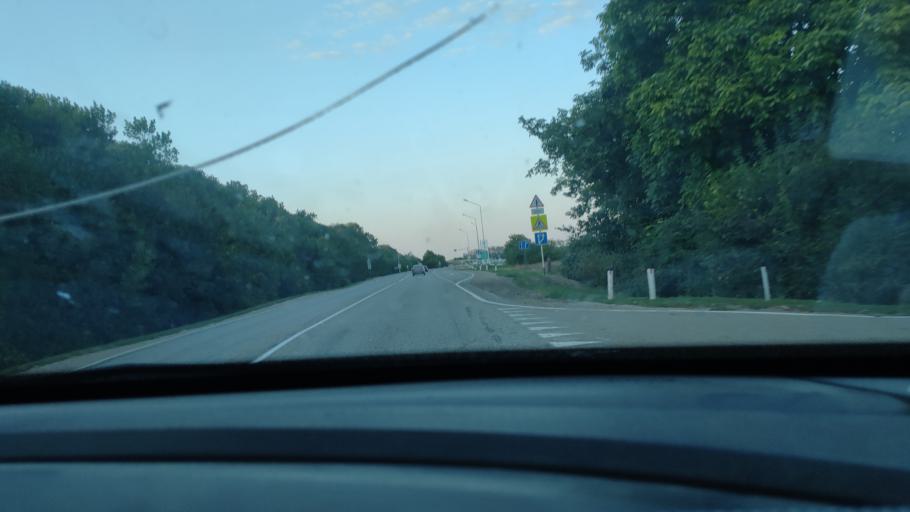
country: RU
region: Krasnodarskiy
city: Novominskaya
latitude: 46.4103
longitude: 39.0038
